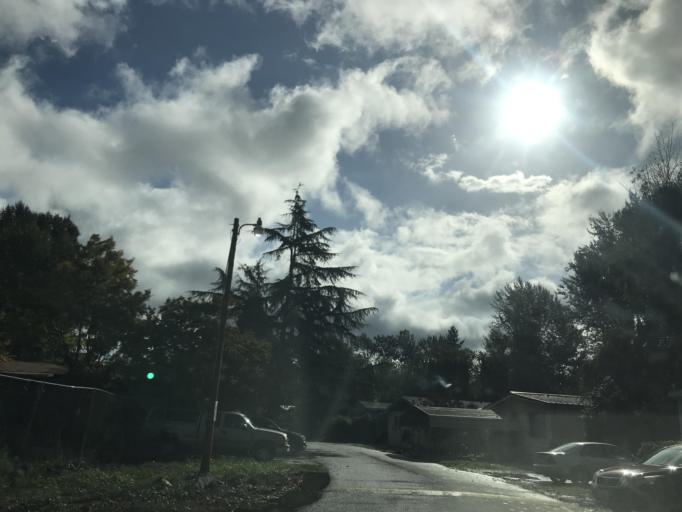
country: US
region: Washington
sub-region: Whatcom County
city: Bellingham
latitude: 48.7866
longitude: -122.4996
